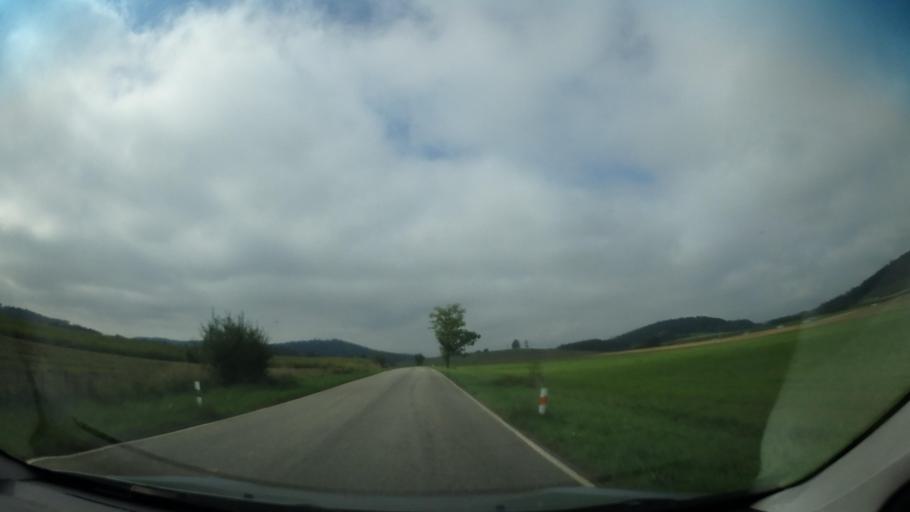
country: CZ
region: Central Bohemia
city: Neveklov
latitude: 49.7412
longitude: 14.5125
